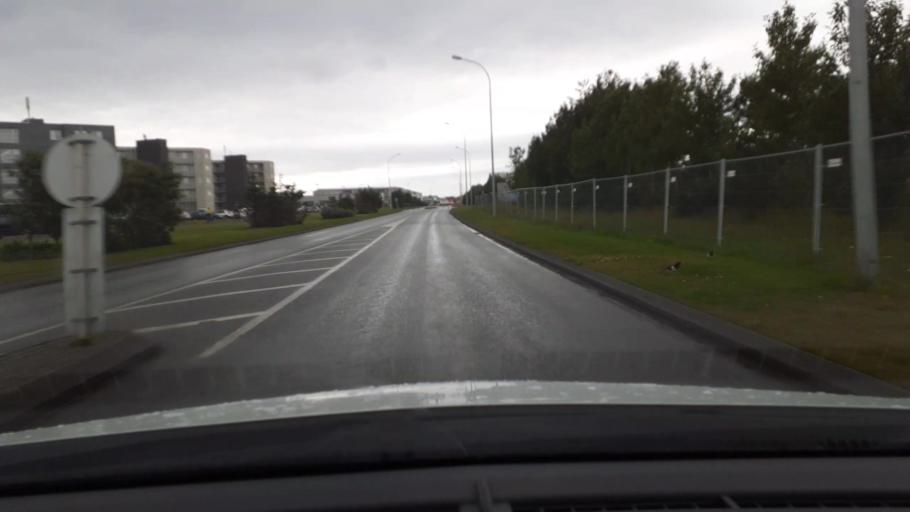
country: IS
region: West
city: Akranes
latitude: 64.3248
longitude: -22.0583
